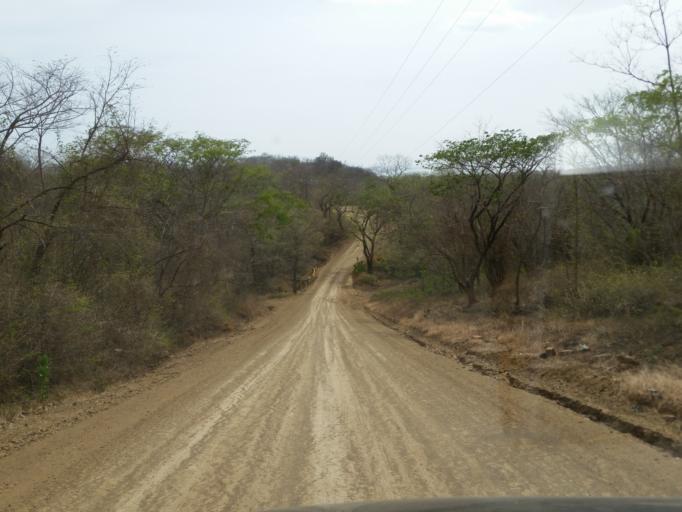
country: NI
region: Rivas
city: Tola
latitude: 11.4453
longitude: -86.0745
